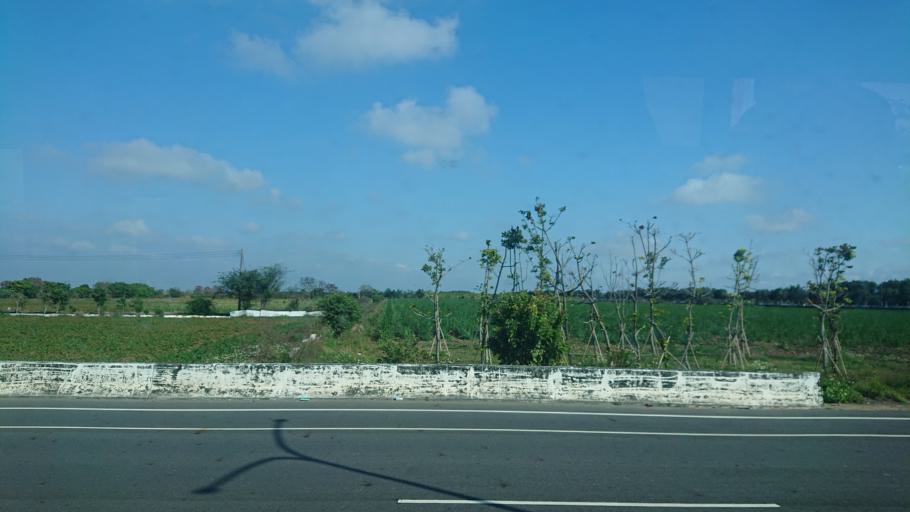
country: TW
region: Taiwan
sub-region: Chiayi
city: Taibao
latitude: 23.4566
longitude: 120.3157
